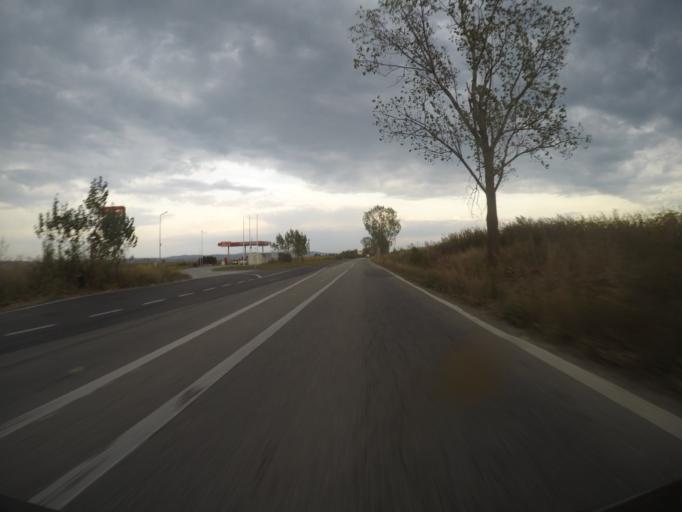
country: RO
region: Sibiu
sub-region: Comuna Sura Mica
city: Sura Mica
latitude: 45.8107
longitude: 24.0758
